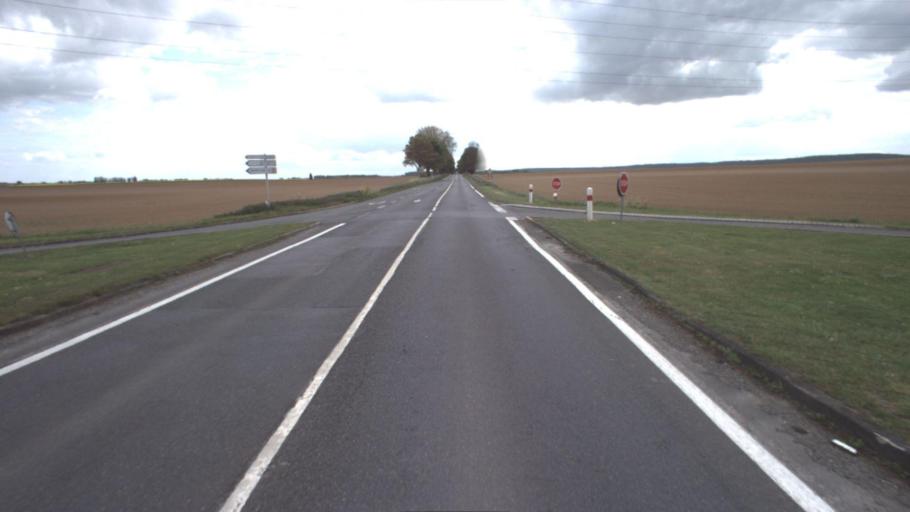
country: FR
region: Picardie
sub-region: Departement de l'Oise
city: Le Plessis-Belleville
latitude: 49.0852
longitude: 2.7569
